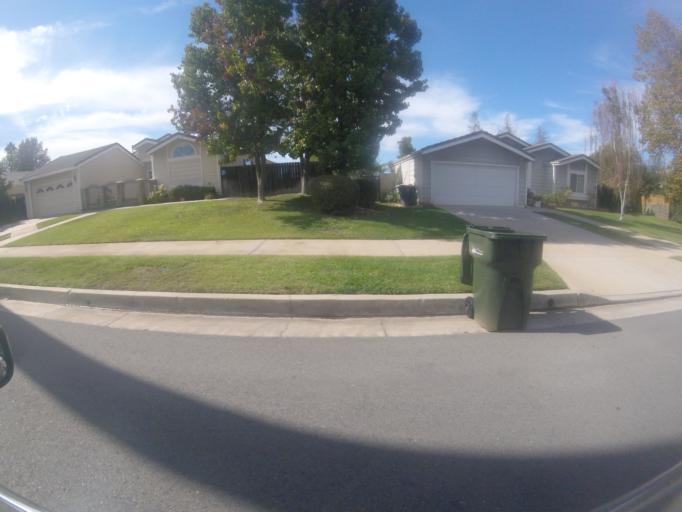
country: US
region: California
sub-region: San Bernardino County
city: Mentone
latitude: 34.0547
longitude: -117.1520
